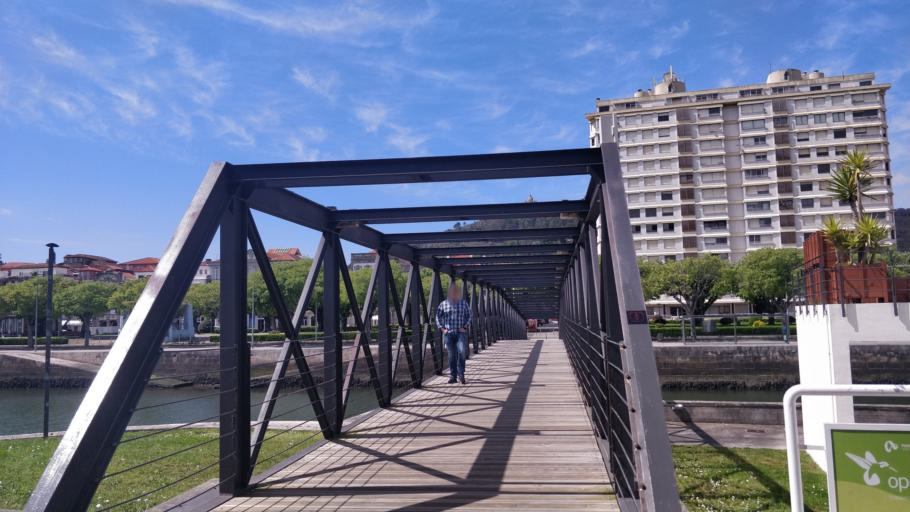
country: PT
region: Viana do Castelo
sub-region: Viana do Castelo
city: Viana do Castelo
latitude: 41.6930
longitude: -8.8235
